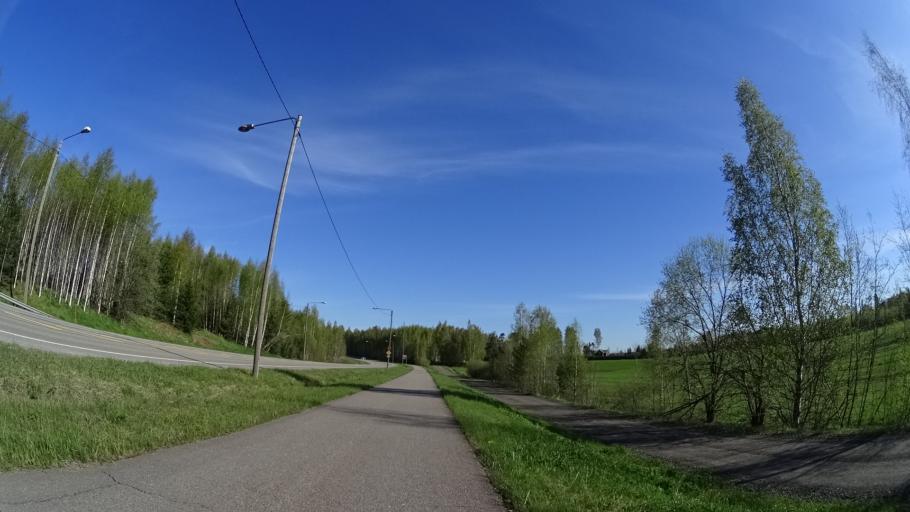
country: FI
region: Uusimaa
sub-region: Helsinki
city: Kilo
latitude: 60.3280
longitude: 24.8257
